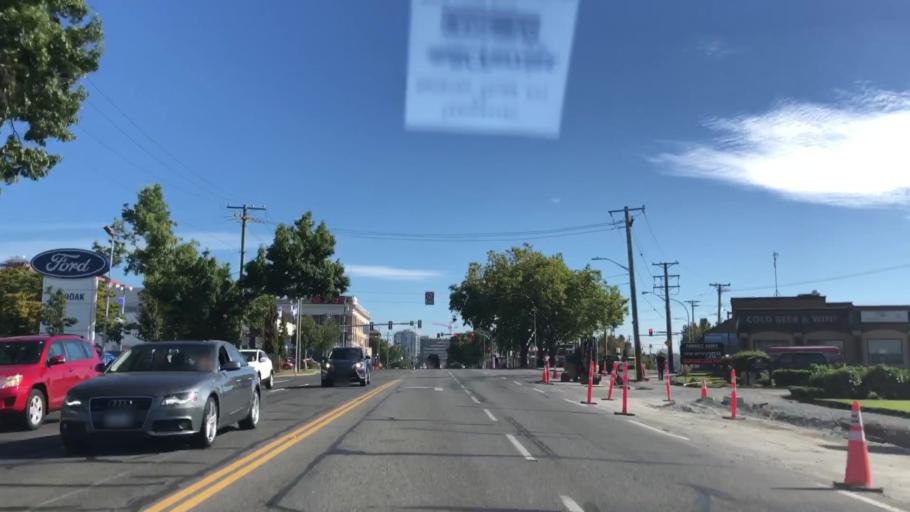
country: CA
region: British Columbia
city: Victoria
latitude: 48.4396
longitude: -123.3677
